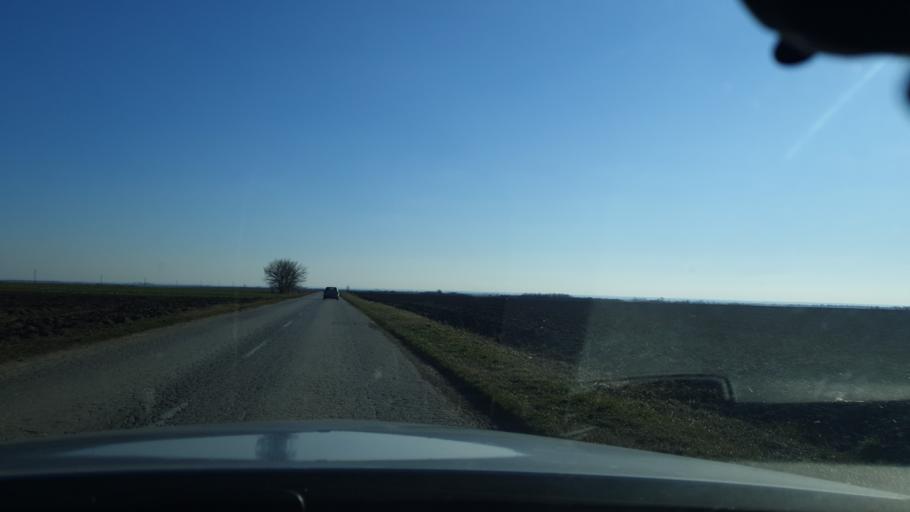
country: RS
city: Vrdnik
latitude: 45.0784
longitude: 19.8081
